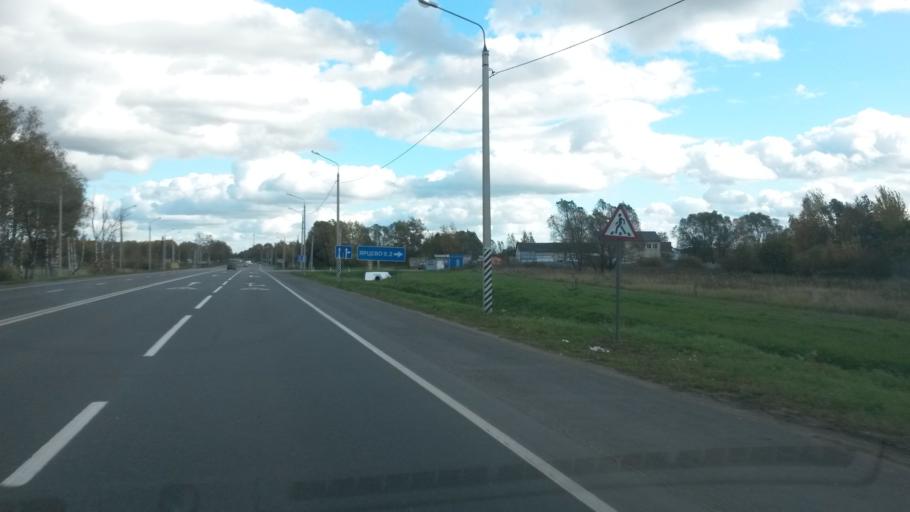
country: RU
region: Jaroslavl
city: Tunoshna
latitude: 57.5392
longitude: 40.0024
